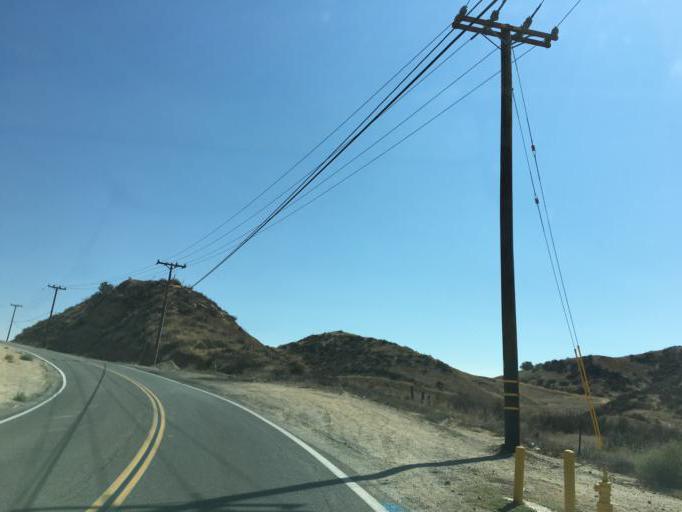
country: US
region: California
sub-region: Los Angeles County
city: Val Verde
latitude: 34.4505
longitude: -118.6511
